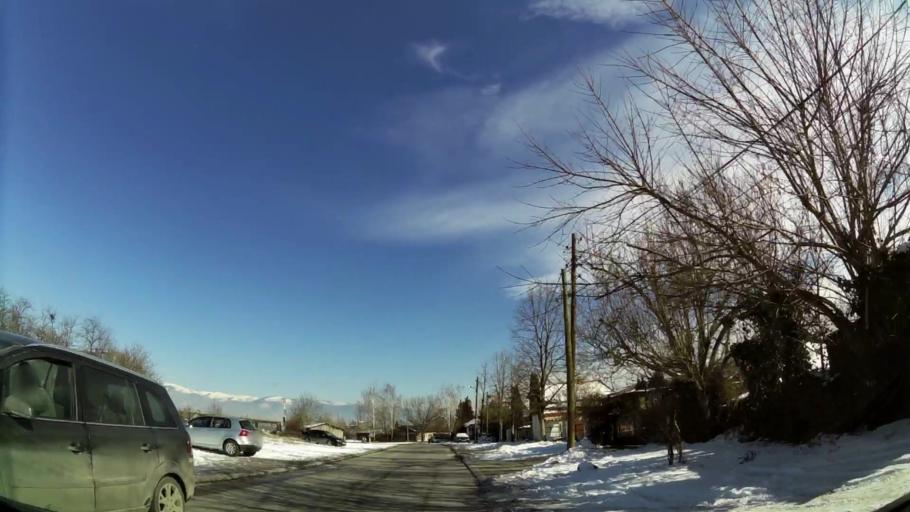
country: MK
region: Saraj
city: Saraj
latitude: 42.0111
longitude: 21.3574
